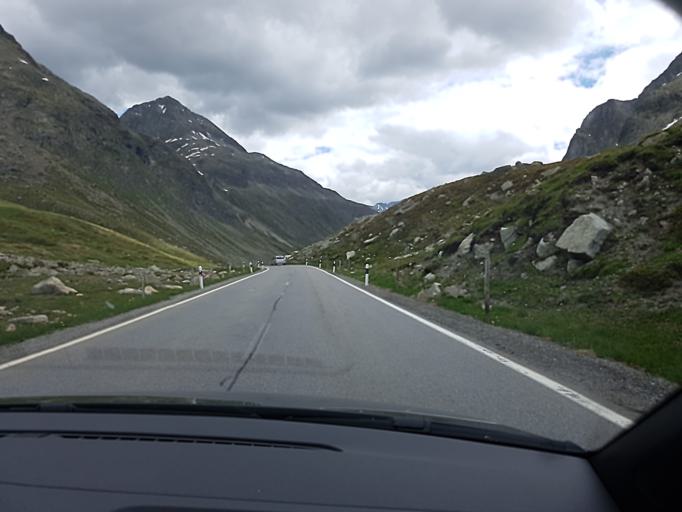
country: CH
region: Grisons
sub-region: Maloja District
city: Silvaplana
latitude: 46.4716
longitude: 9.7319
